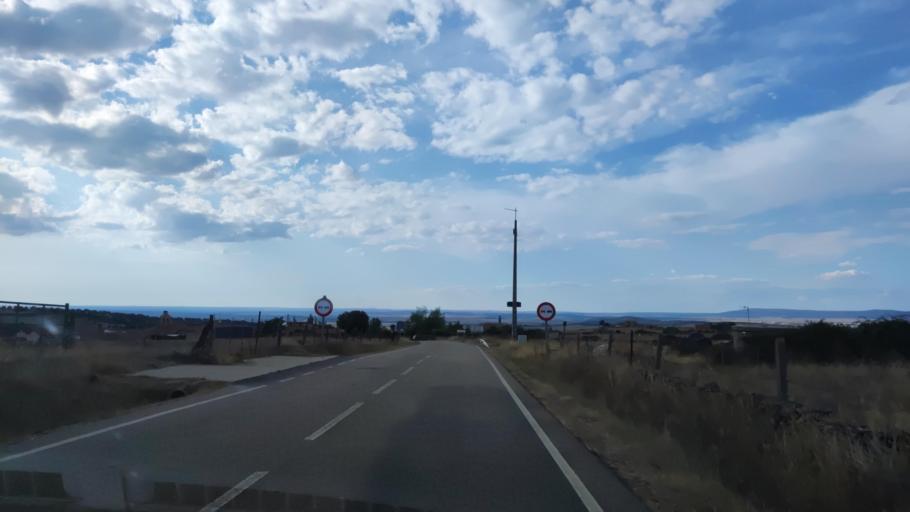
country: ES
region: Castille and Leon
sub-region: Provincia de Salamanca
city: Pastores
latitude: 40.5135
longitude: -6.5063
